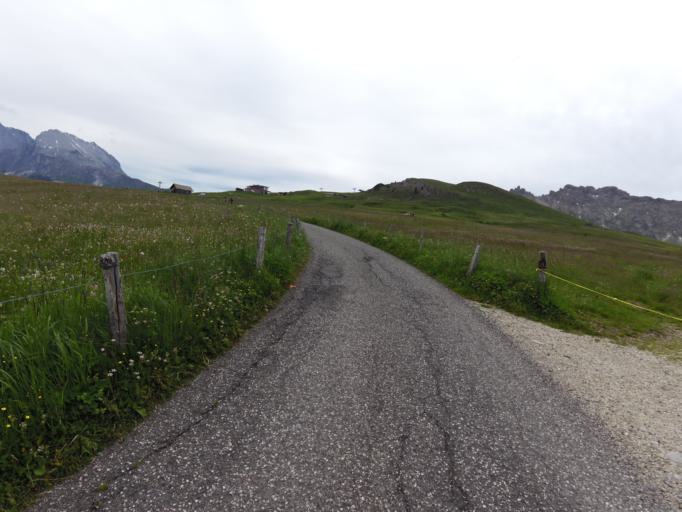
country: IT
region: Trentino-Alto Adige
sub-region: Bolzano
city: Ortisei
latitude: 46.5247
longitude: 11.6324
